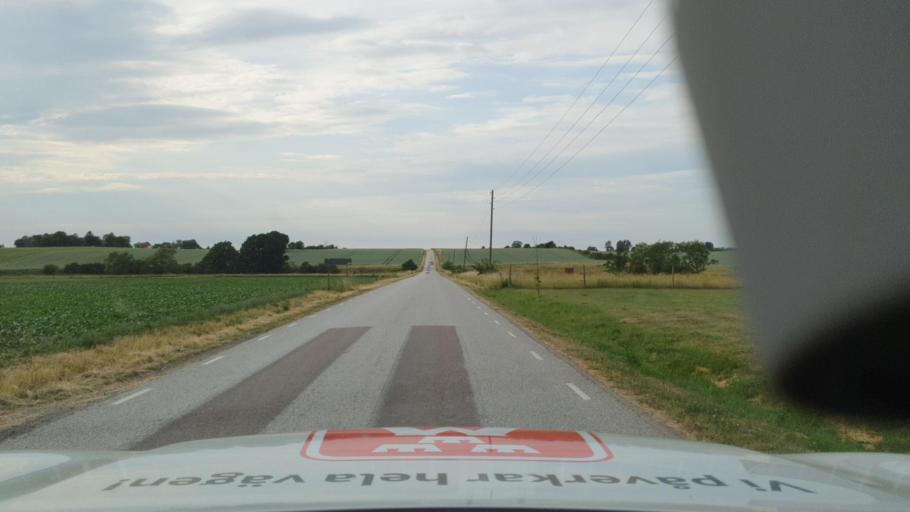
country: SE
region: Skane
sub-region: Sjobo Kommun
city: Sjoebo
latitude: 55.6435
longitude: 13.8163
